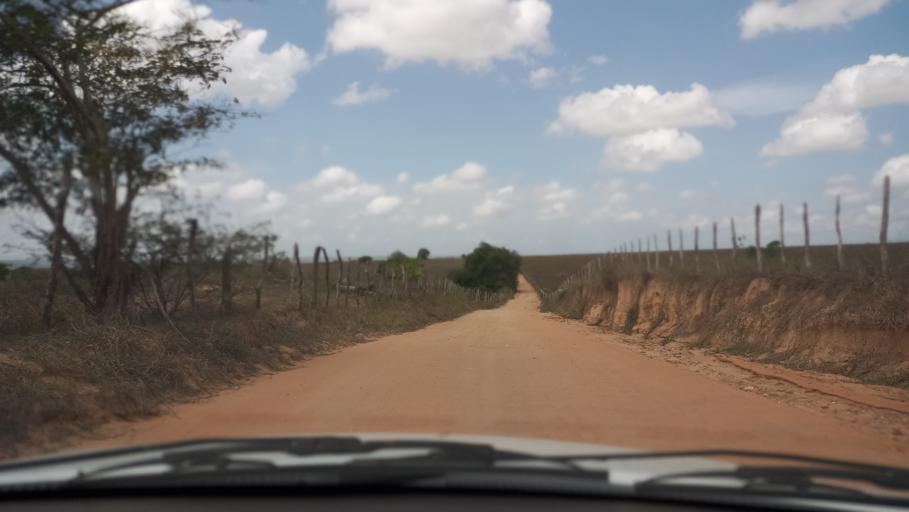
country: BR
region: Rio Grande do Norte
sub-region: Montanhas
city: Montanhas
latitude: -6.3566
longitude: -35.3370
